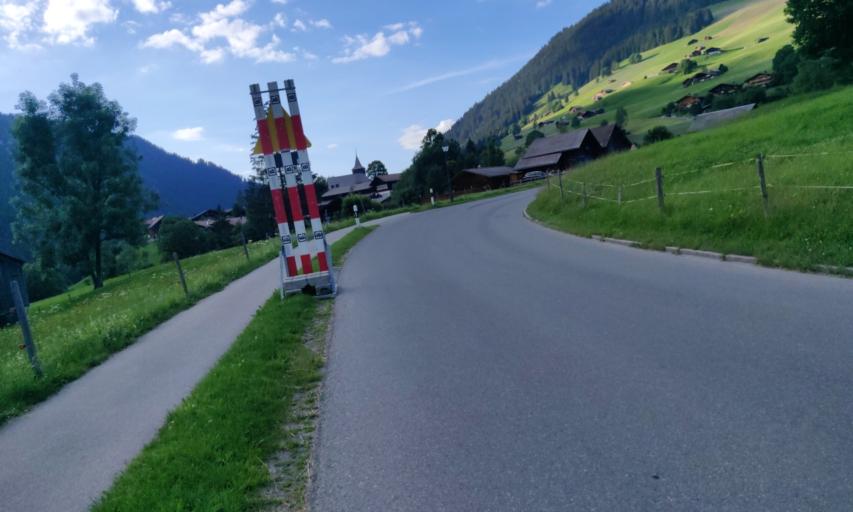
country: CH
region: Bern
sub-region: Obersimmental-Saanen District
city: Gstaad
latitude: 46.4217
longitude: 7.3223
